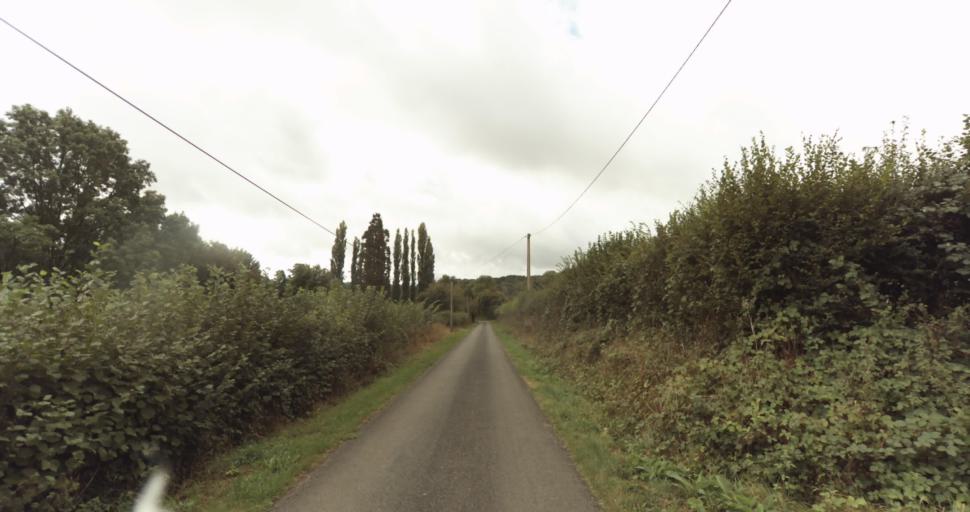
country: FR
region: Lower Normandy
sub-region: Departement de l'Orne
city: Gace
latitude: 48.8537
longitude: 0.2838
